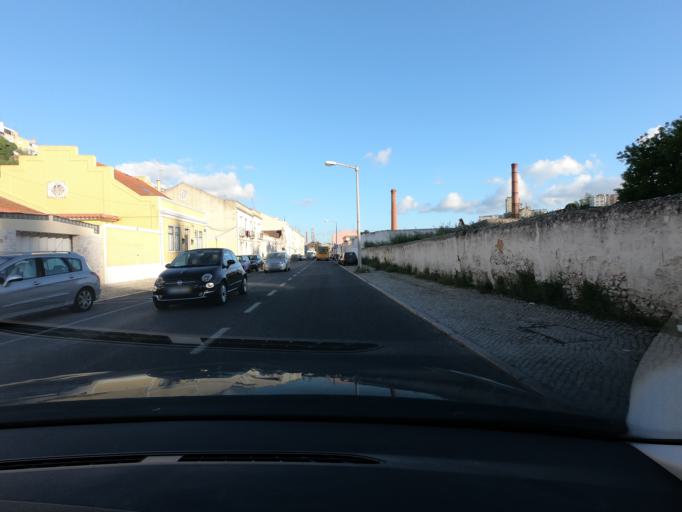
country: PT
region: Lisbon
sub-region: Lisbon
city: Lisbon
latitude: 38.7304
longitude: -9.1163
